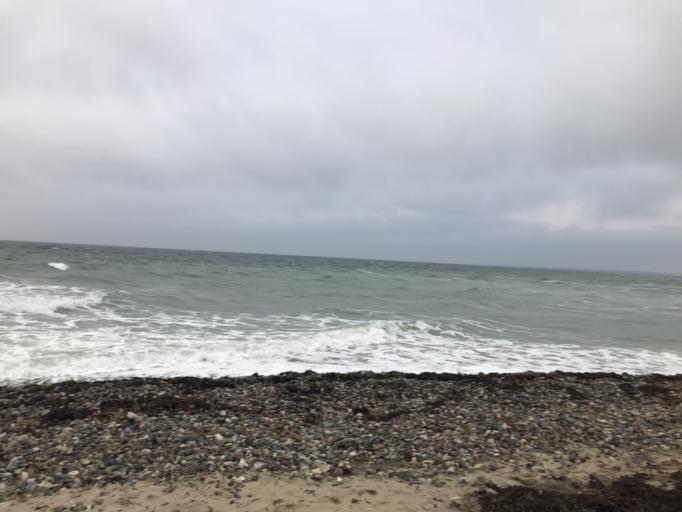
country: DK
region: South Denmark
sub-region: Haderslev Kommune
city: Starup
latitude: 55.1839
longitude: 9.6579
